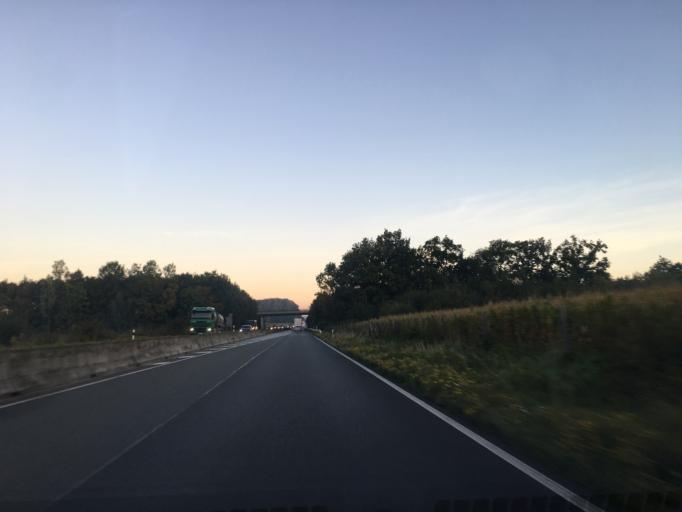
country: DE
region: North Rhine-Westphalia
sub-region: Regierungsbezirk Munster
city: Altenberge
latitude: 52.0125
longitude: 7.5023
